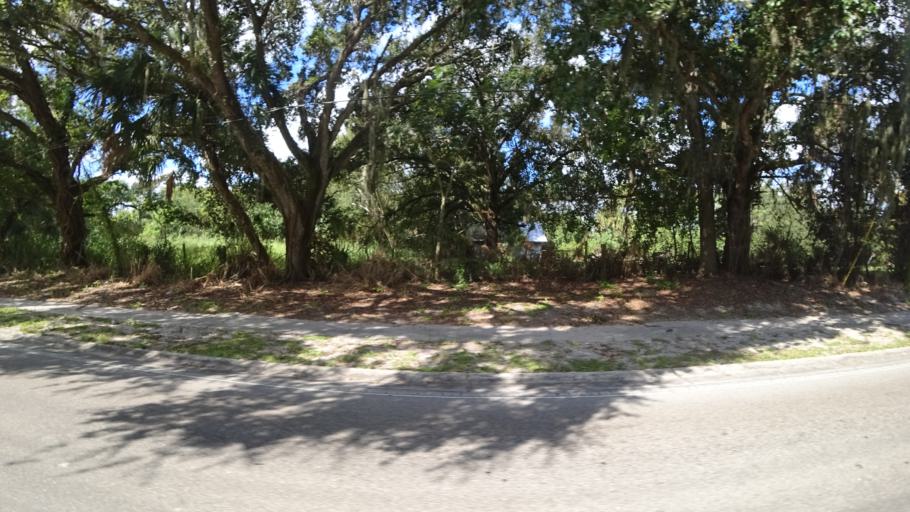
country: US
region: Florida
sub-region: Manatee County
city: Samoset
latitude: 27.4865
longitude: -82.5303
